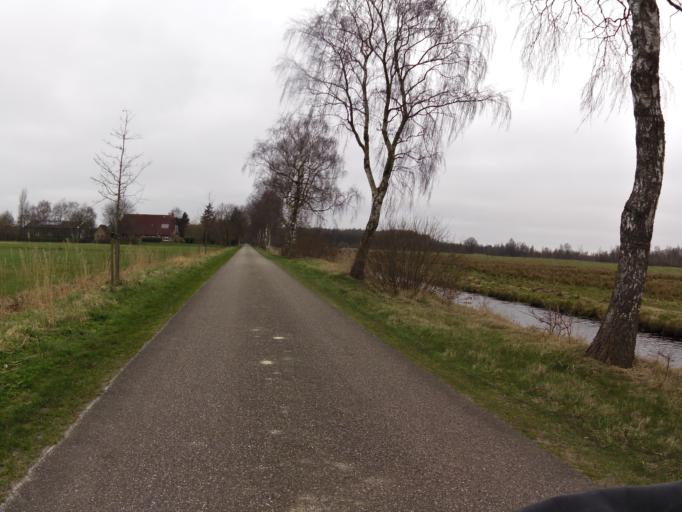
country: NL
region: Drenthe
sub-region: Gemeente Westerveld
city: Dwingeloo
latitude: 52.9781
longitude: 6.4084
